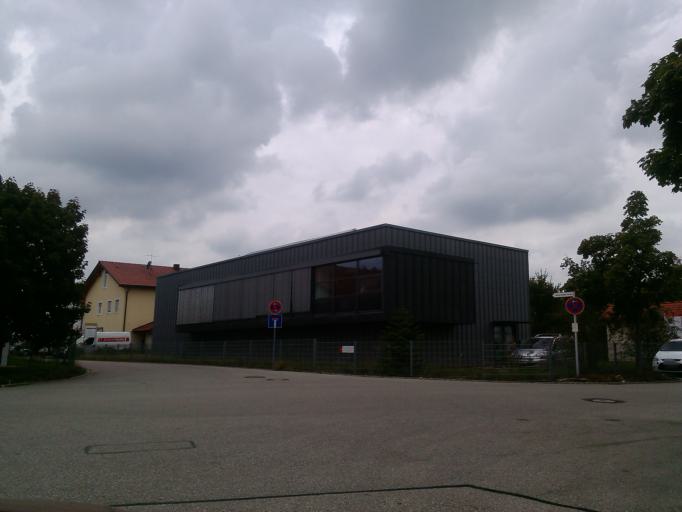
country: DE
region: Bavaria
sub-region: Upper Bavaria
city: Gauting
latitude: 48.0952
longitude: 11.3645
